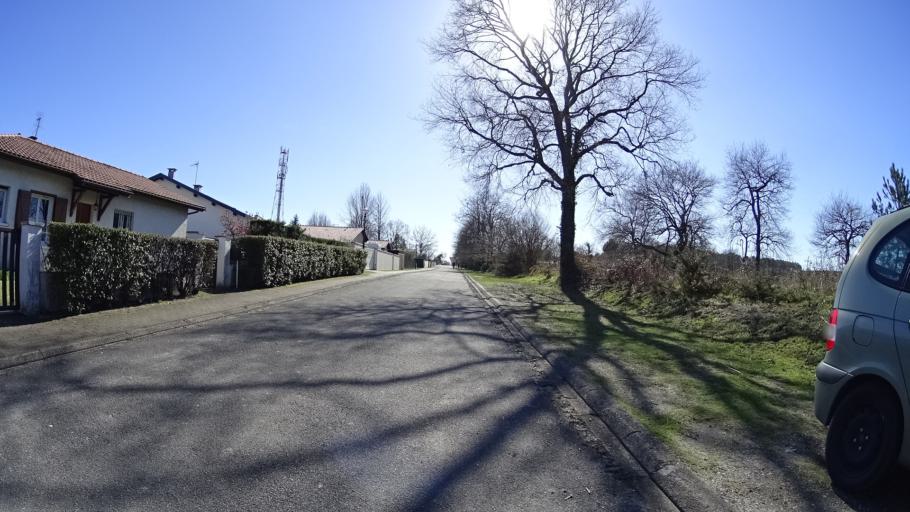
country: FR
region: Aquitaine
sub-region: Departement des Landes
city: Saint-Paul-les-Dax
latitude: 43.7347
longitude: -1.0839
